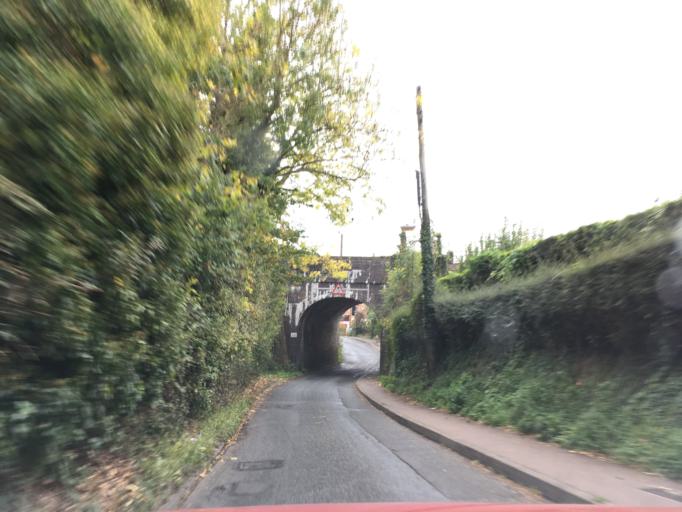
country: GB
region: England
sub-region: Gloucestershire
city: Stonehouse
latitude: 51.7434
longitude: -2.2551
